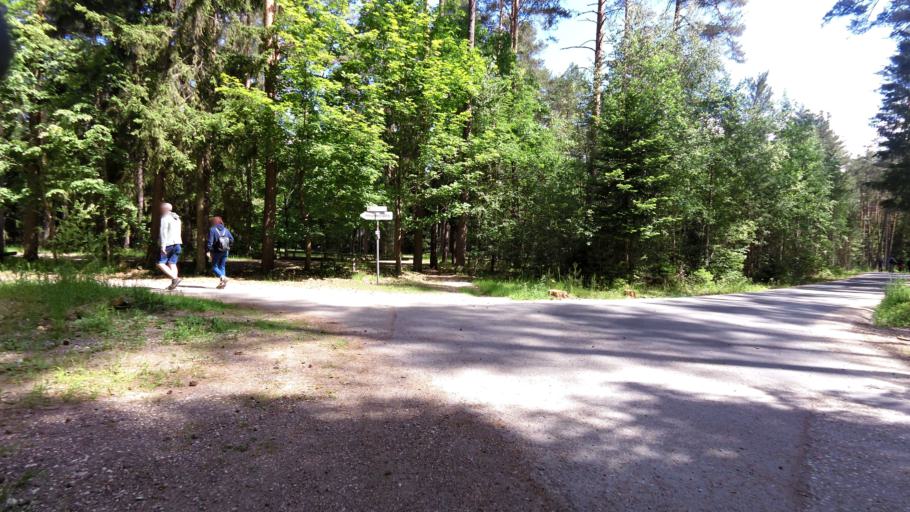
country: DE
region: Bavaria
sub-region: Regierungsbezirk Mittelfranken
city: Pleinfeld
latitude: 49.1176
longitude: 10.9629
